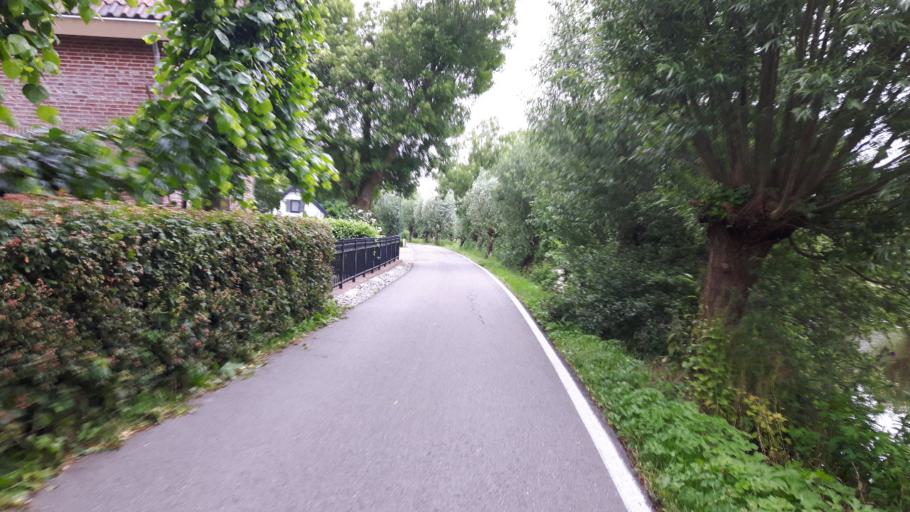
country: NL
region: Utrecht
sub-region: Gemeente Oudewater
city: Oudewater
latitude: 52.0379
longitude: 4.8877
